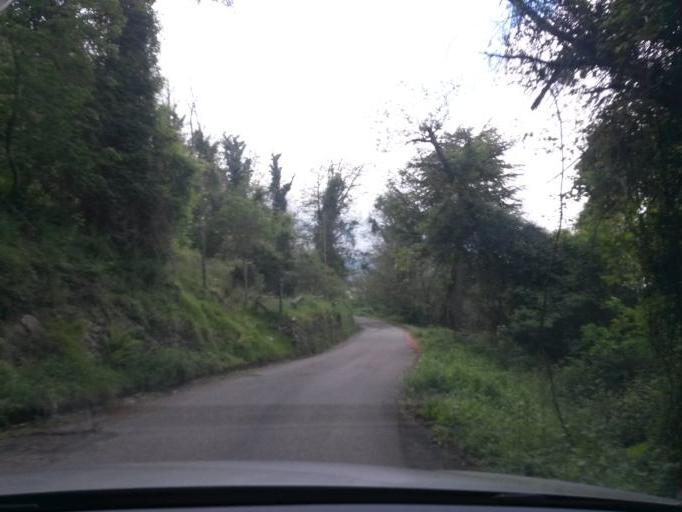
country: IT
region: Tuscany
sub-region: Provincia di Livorno
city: Marciana Marina
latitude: 42.7803
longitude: 10.1994
